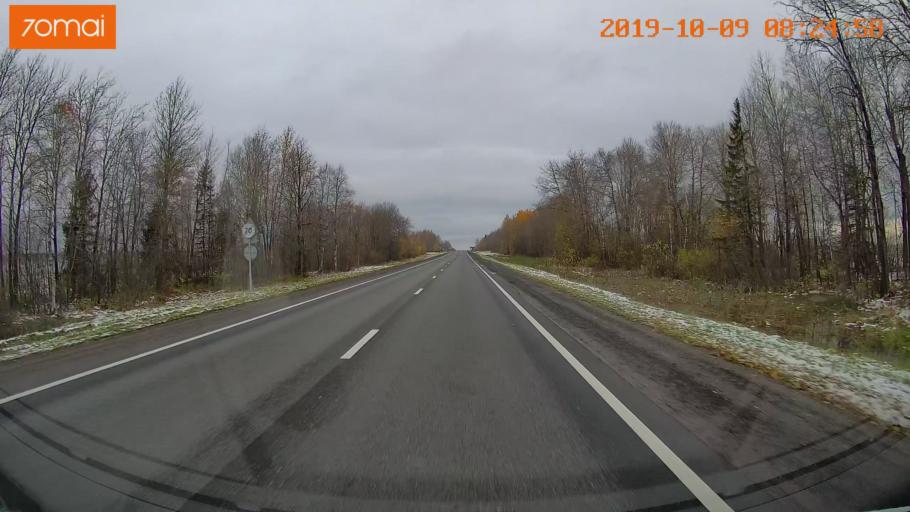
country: RU
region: Vologda
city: Gryazovets
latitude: 58.7739
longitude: 40.2753
